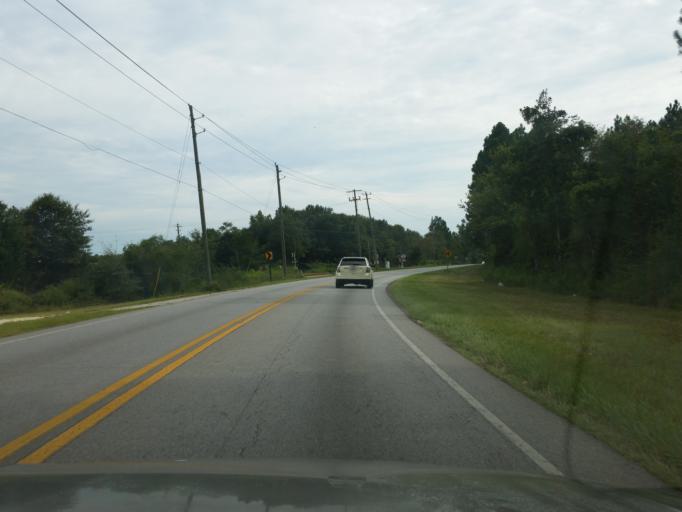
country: US
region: Florida
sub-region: Escambia County
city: Cantonment
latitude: 30.6448
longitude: -87.3172
